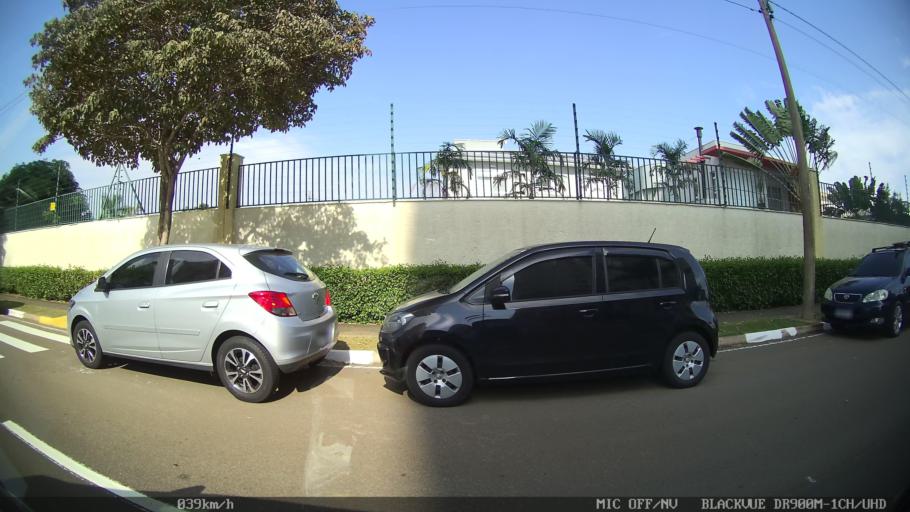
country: BR
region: Sao Paulo
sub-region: Paulinia
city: Paulinia
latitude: -22.7754
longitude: -47.1497
